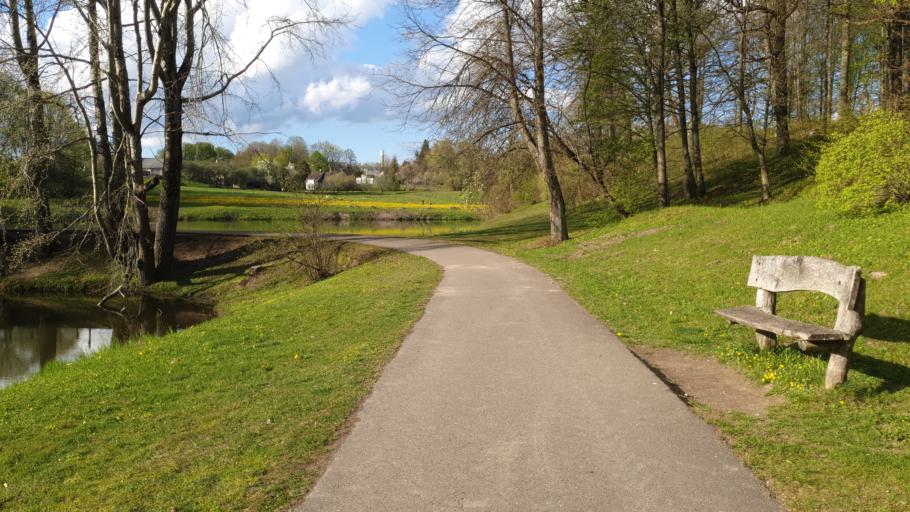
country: LT
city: Gelgaudiskis
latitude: 55.0984
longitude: 22.9885
